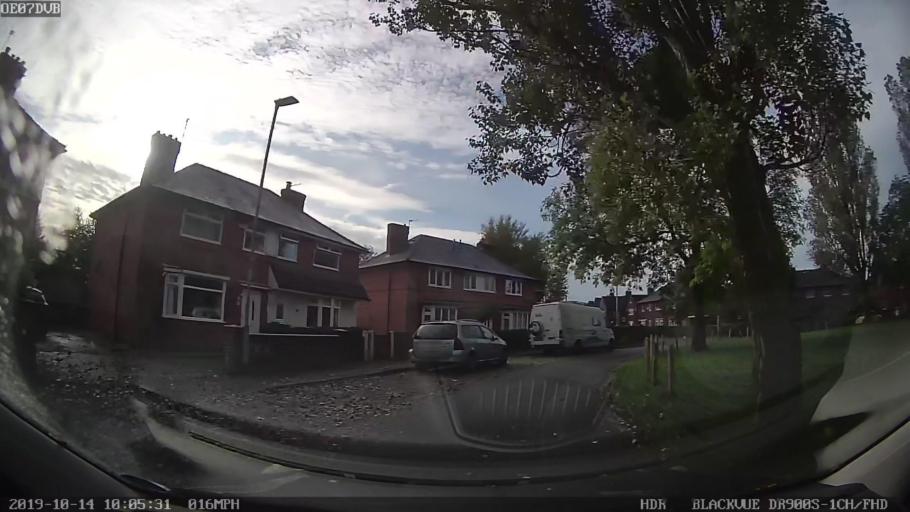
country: GB
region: England
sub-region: Manchester
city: Blackley
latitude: 53.5257
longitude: -2.1924
